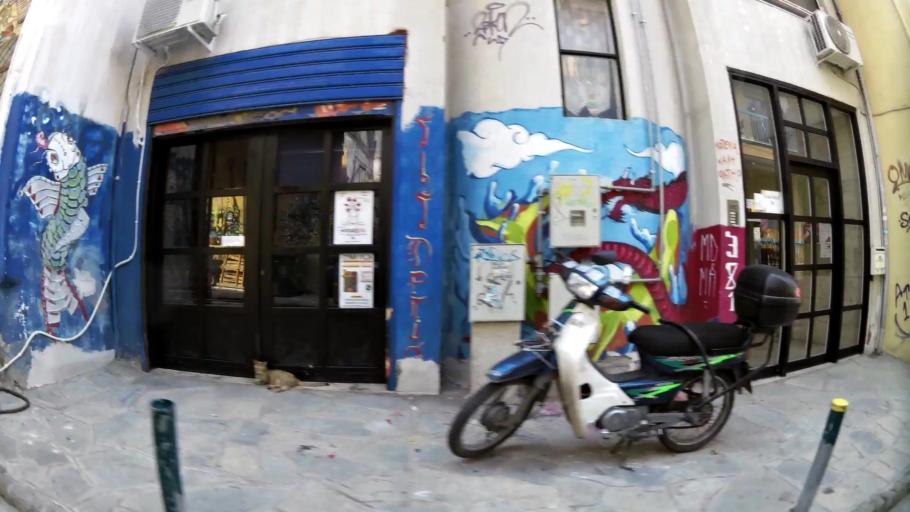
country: GR
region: Central Macedonia
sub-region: Nomos Thessalonikis
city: Sykies
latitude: 40.6432
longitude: 22.9464
